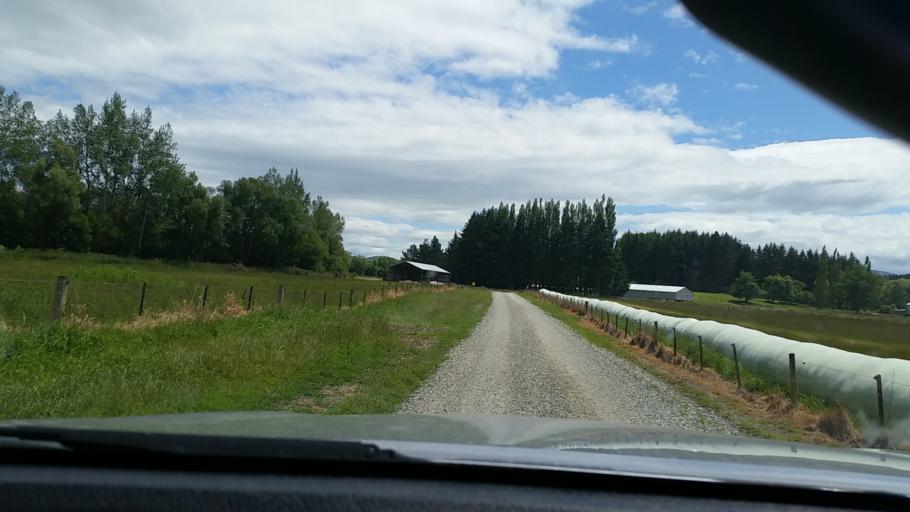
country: NZ
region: Otago
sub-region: Queenstown-Lakes District
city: Kingston
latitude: -45.7419
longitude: 168.5749
